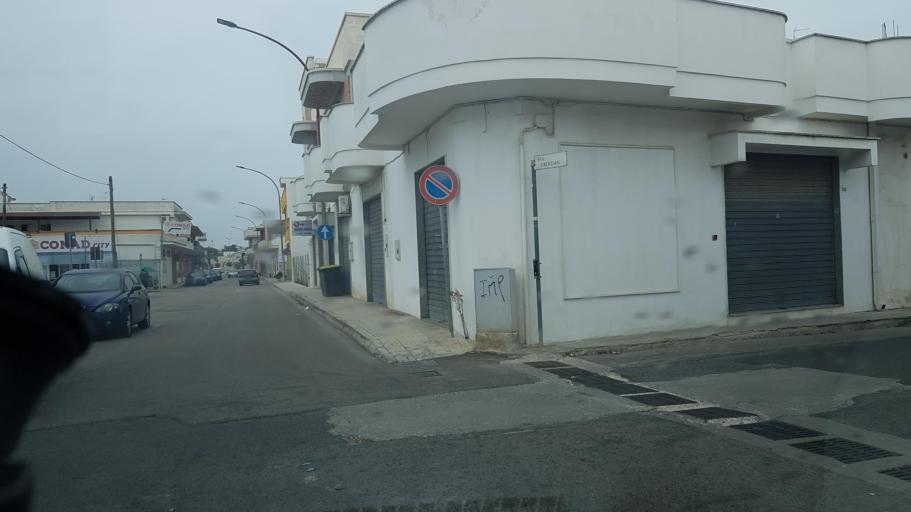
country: IT
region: Apulia
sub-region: Provincia di Lecce
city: Leverano
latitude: 40.2865
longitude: 17.9964
